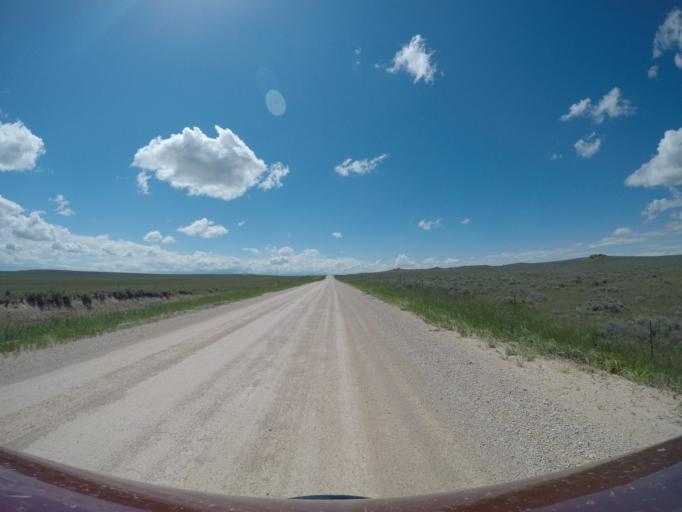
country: US
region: Wyoming
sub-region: Park County
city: Powell
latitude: 45.2051
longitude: -108.7496
